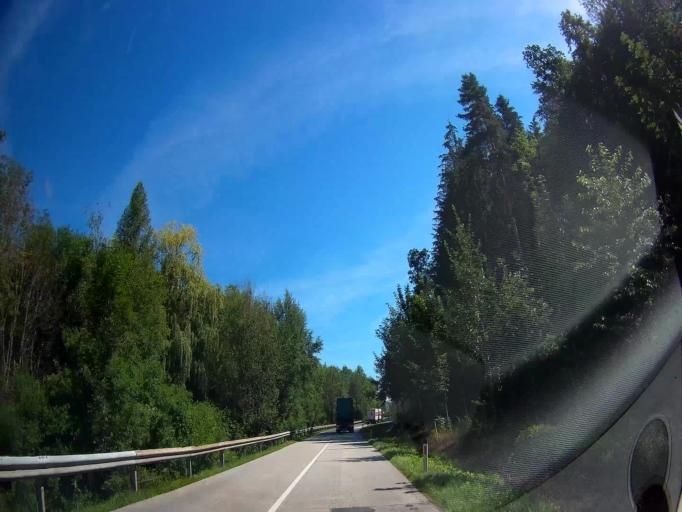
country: AT
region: Carinthia
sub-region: Politischer Bezirk Sankt Veit an der Glan
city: Sankt Veit an der Glan
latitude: 46.7289
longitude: 14.3862
